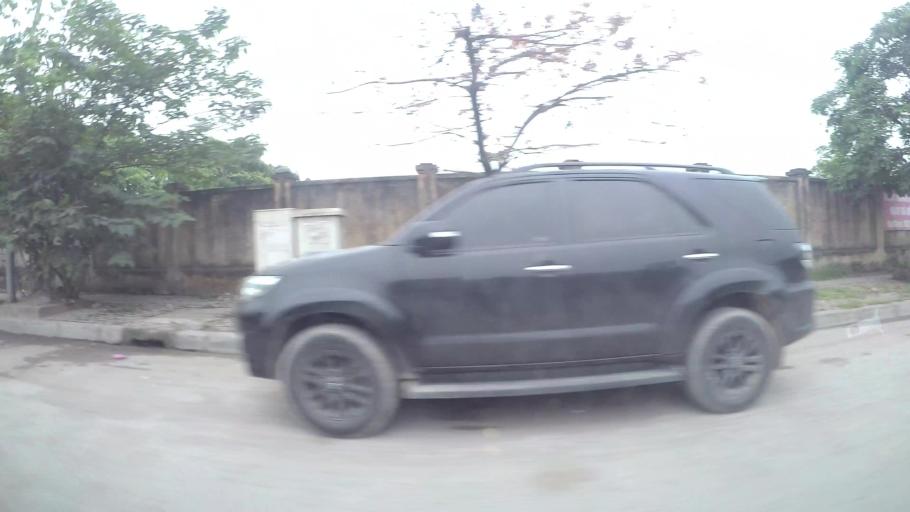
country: VN
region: Ha Noi
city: Hai BaTrung
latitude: 20.9818
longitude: 105.8905
